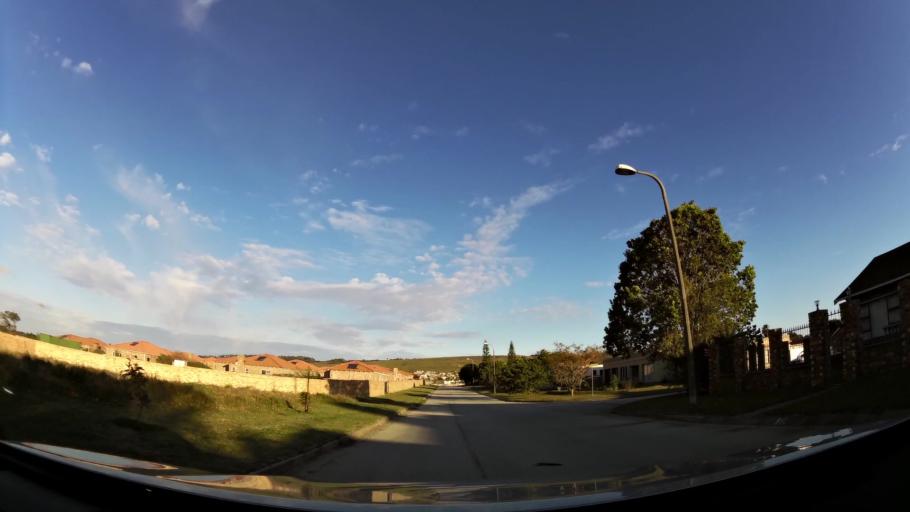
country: ZA
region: Eastern Cape
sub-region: Nelson Mandela Bay Metropolitan Municipality
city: Port Elizabeth
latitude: -33.9753
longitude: 25.4927
